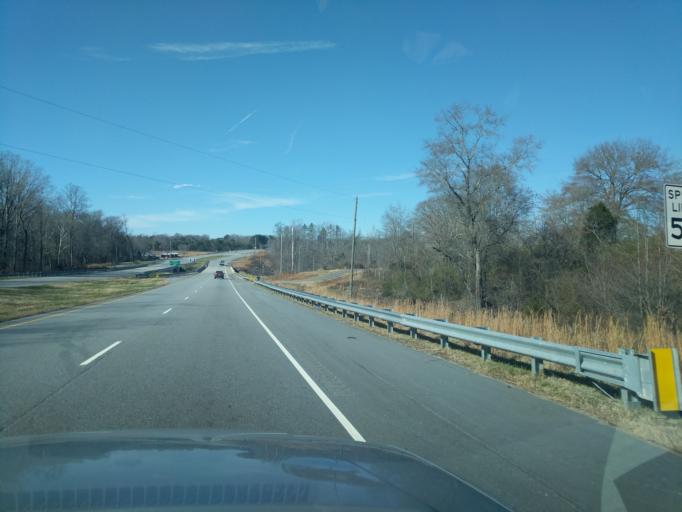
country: US
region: North Carolina
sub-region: Rutherford County
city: Forest City
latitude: 35.2448
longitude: -81.8648
